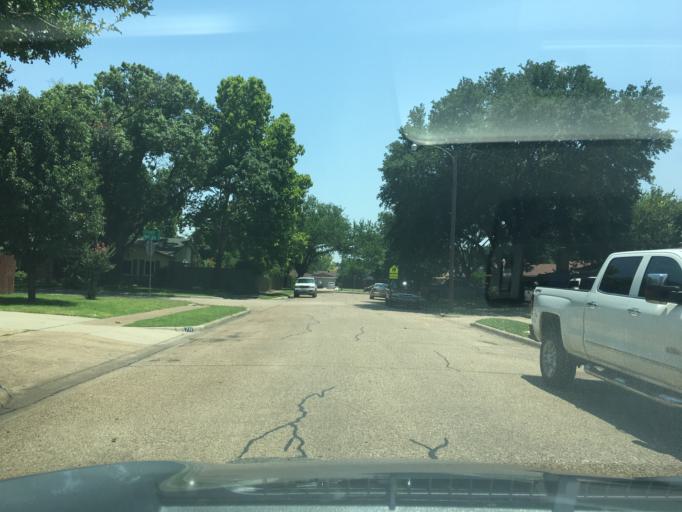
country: US
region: Texas
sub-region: Dallas County
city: Richardson
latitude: 32.9196
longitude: -96.7052
